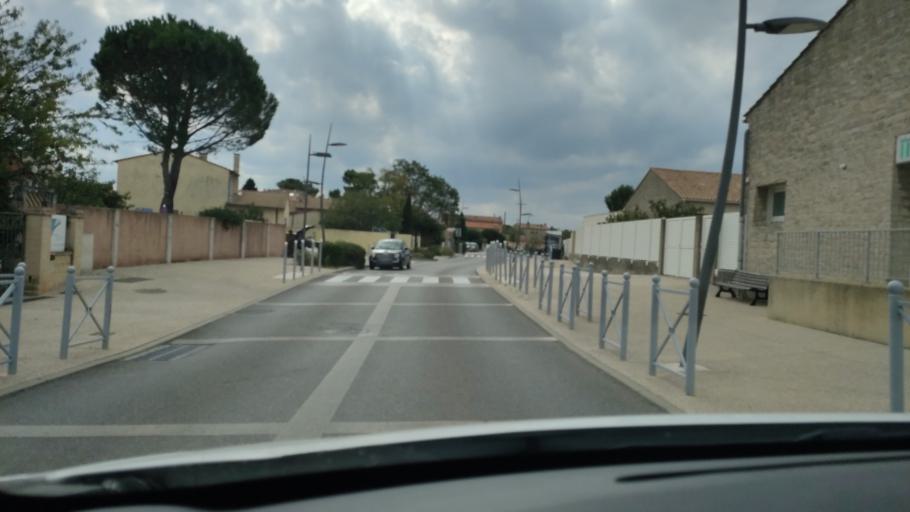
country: FR
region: Languedoc-Roussillon
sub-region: Departement du Gard
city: Les Angles
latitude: 43.9624
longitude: 4.7700
